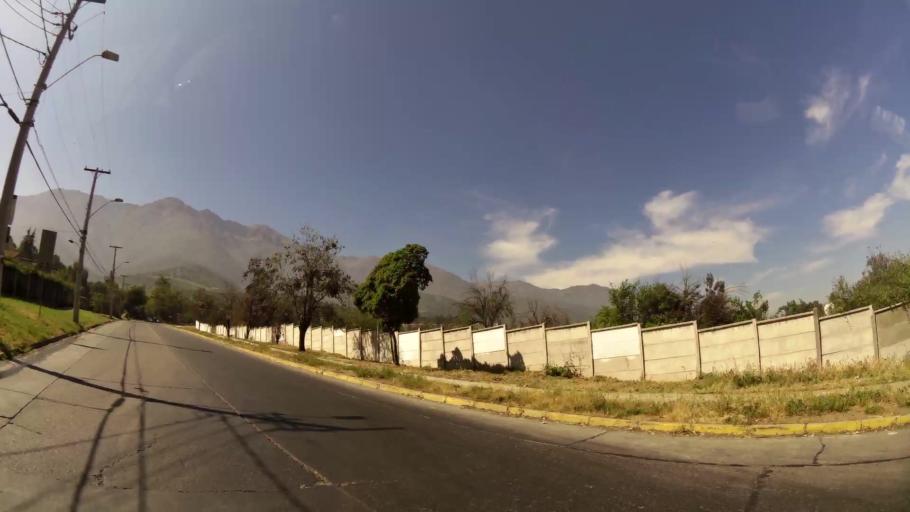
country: CL
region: Santiago Metropolitan
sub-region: Provincia de Santiago
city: Villa Presidente Frei, Nunoa, Santiago, Chile
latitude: -33.4596
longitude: -70.5230
